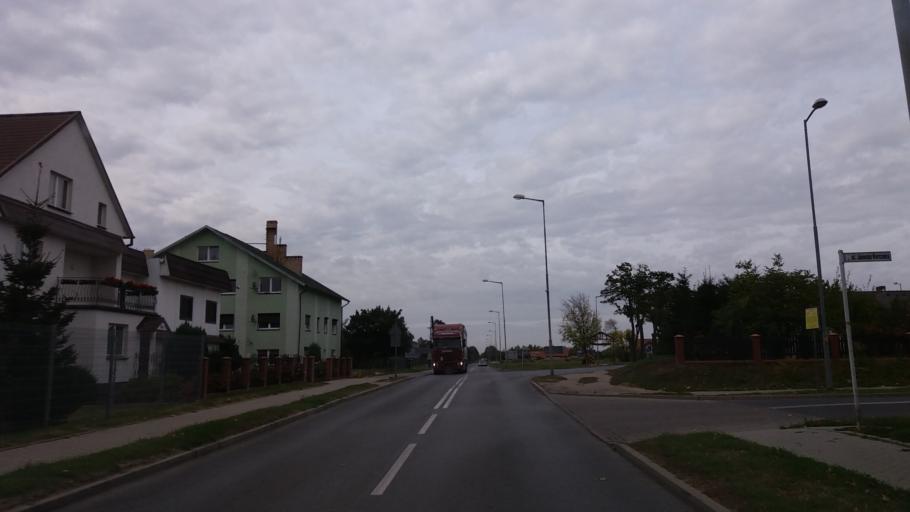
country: PL
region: Lubusz
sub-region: Powiat strzelecko-drezdenecki
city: Strzelce Krajenskie
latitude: 52.8813
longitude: 15.5223
